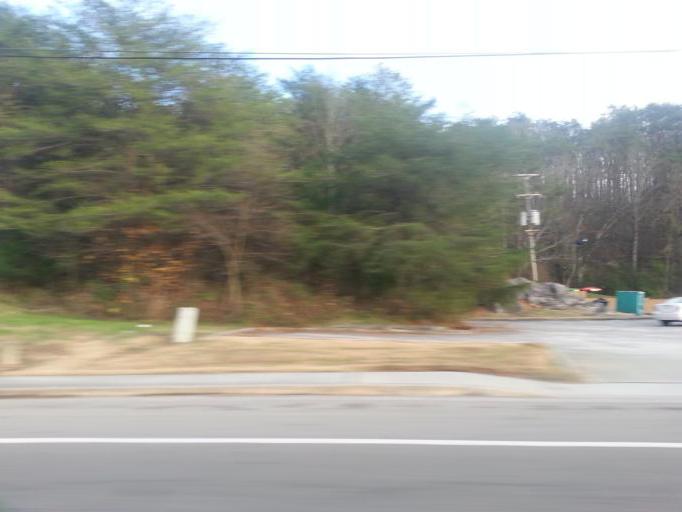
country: US
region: Tennessee
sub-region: Rhea County
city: Dayton
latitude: 35.5094
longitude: -84.9991
